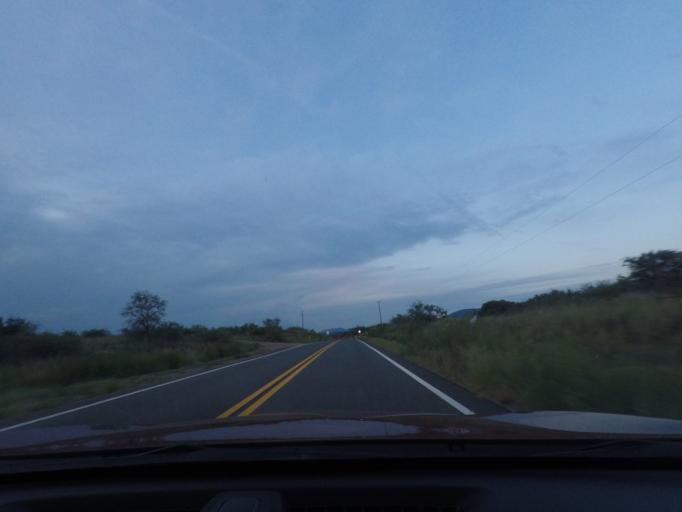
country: US
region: Arizona
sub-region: Yavapai County
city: Prescott
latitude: 34.4971
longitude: -112.6857
